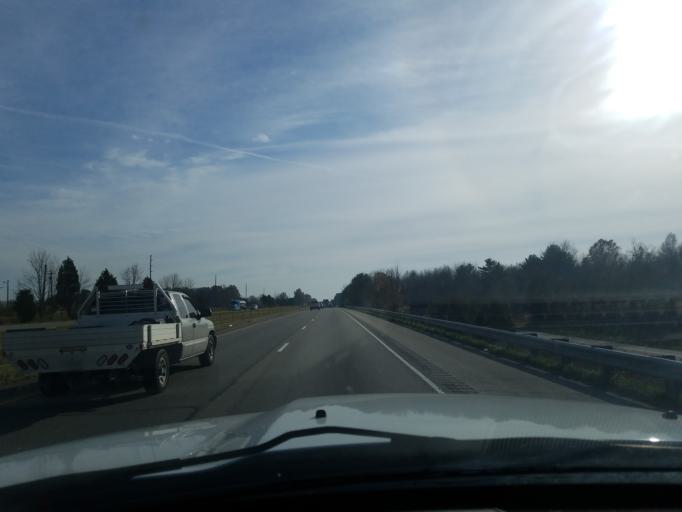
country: US
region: Indiana
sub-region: Bartholomew County
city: Columbus
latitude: 39.1571
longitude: -85.9589
